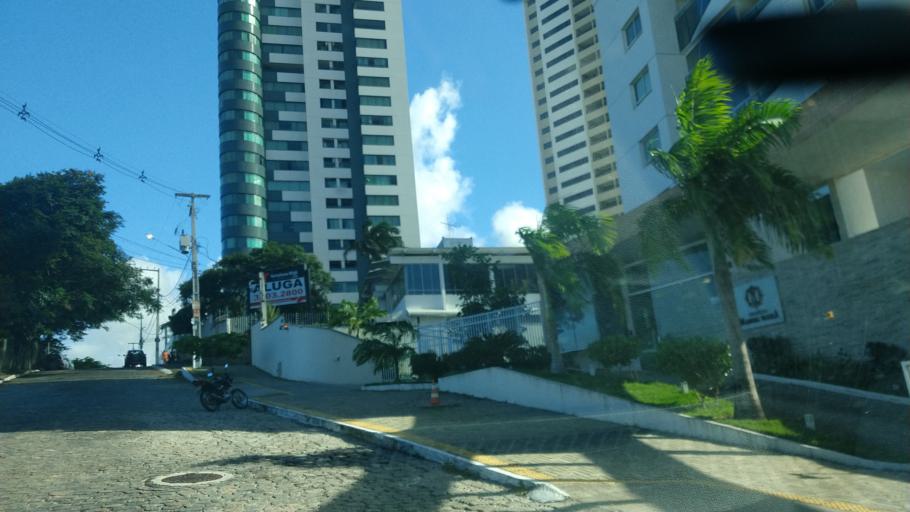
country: BR
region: Rio Grande do Norte
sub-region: Natal
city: Natal
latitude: -5.8295
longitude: -35.2181
